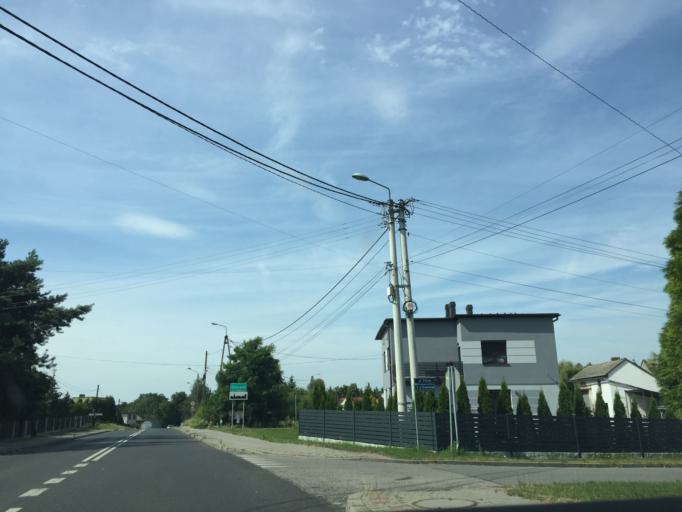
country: PL
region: Silesian Voivodeship
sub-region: Powiat wodzislawski
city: Gorzyce
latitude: 49.9545
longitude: 18.4011
